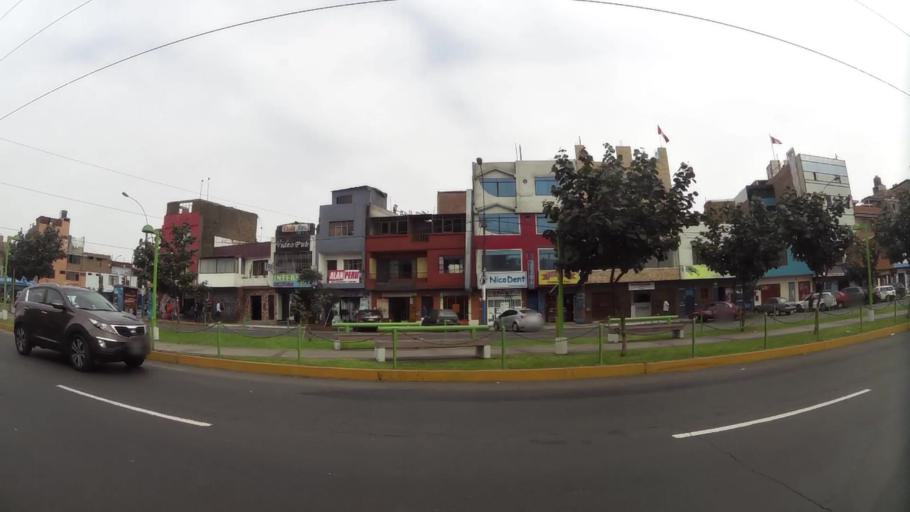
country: PE
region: Callao
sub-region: Callao
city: Callao
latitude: -12.0305
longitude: -77.0889
